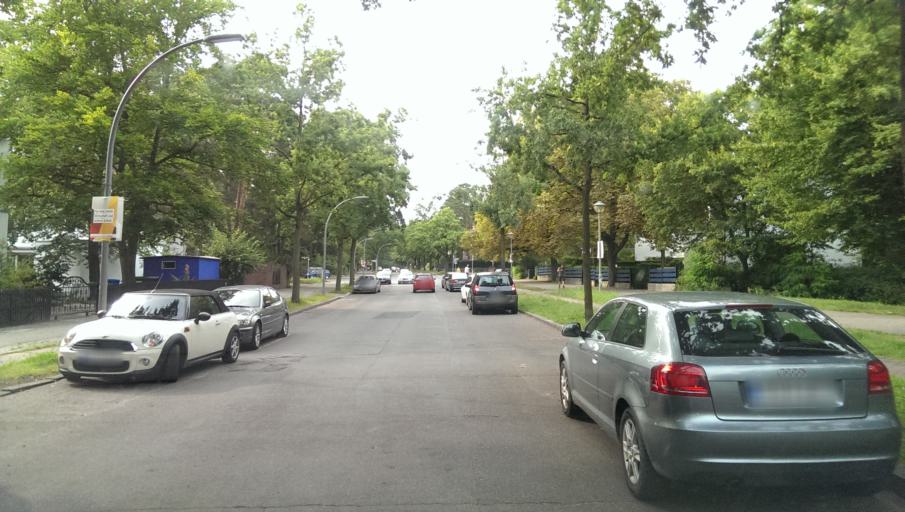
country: DE
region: Berlin
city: Zehlendorf Bezirk
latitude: 52.4441
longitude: 13.2376
